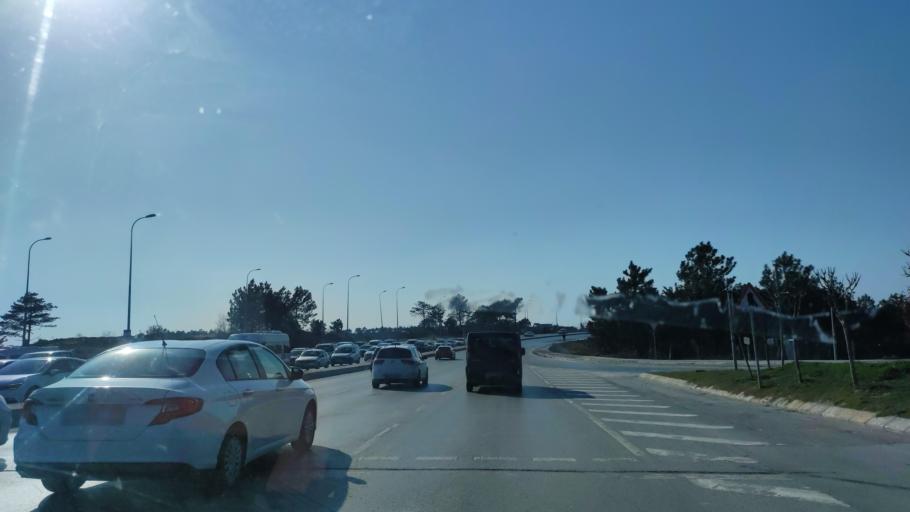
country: TR
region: Istanbul
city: Basaksehir
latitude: 41.1742
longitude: 28.7535
